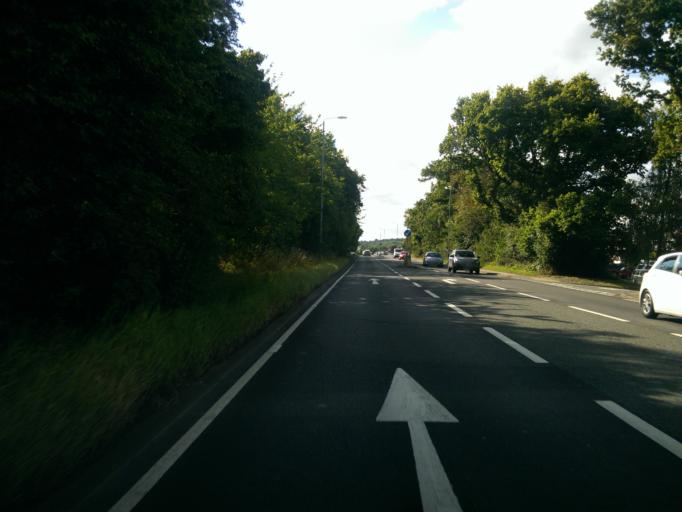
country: GB
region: England
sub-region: Warwickshire
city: Atherstone
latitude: 52.5886
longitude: -1.5841
